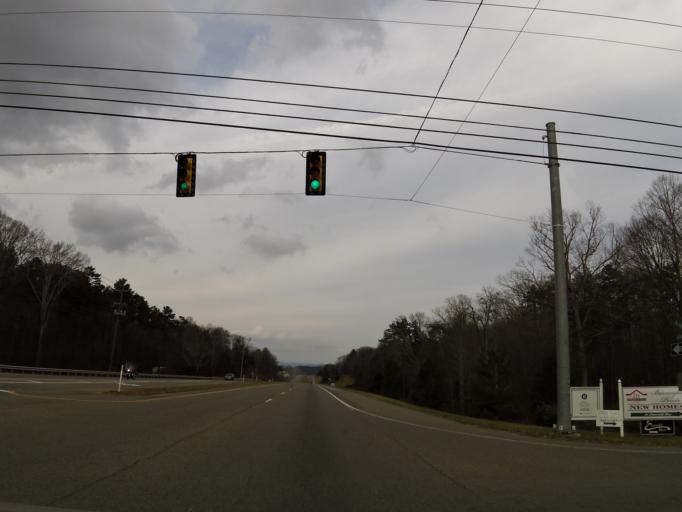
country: US
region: Tennessee
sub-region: Hamilton County
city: Sale Creek
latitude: 35.3171
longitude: -85.1383
